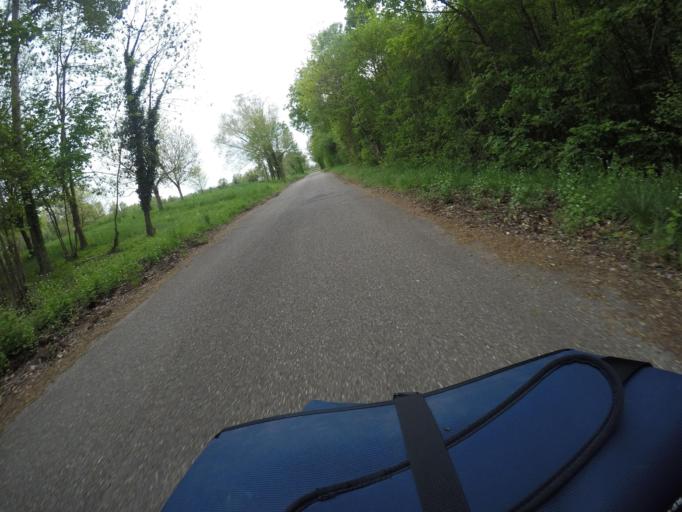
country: FR
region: Alsace
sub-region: Departement du Bas-Rhin
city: Plobsheim
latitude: 48.5003
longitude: 7.7731
